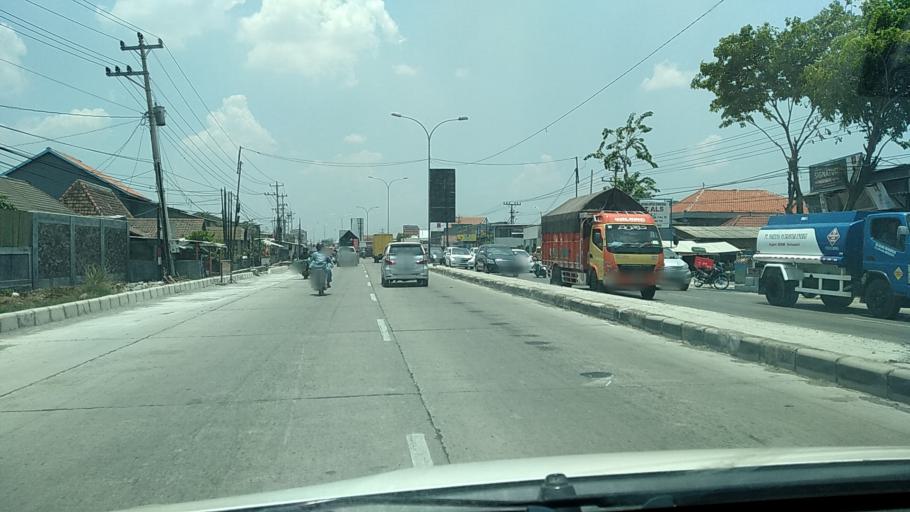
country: ID
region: Central Java
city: Semarang
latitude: -6.9556
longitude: 110.4674
